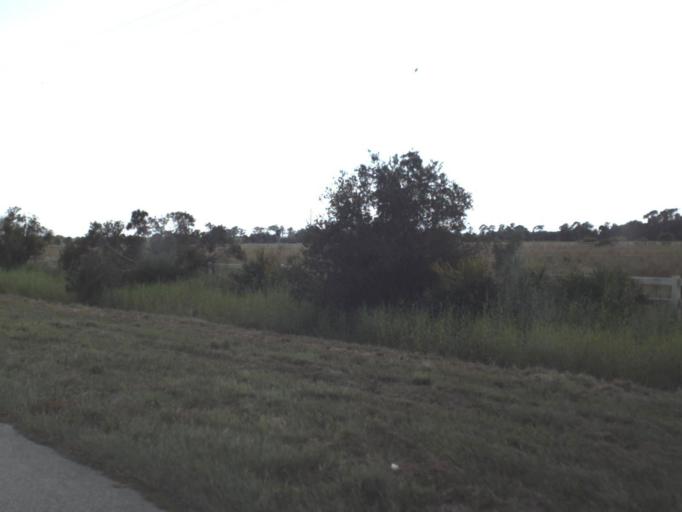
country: US
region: Florida
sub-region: Okeechobee County
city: Okeechobee
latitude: 27.2893
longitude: -80.8854
